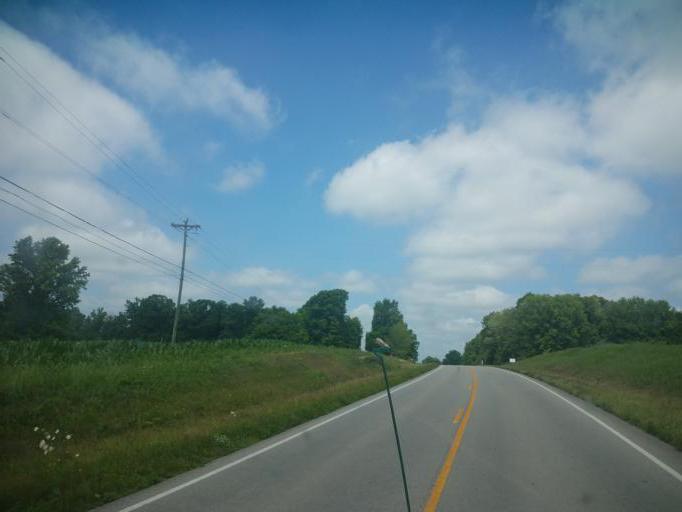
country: US
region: Kentucky
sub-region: Metcalfe County
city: Edmonton
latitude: 36.8955
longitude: -85.7325
